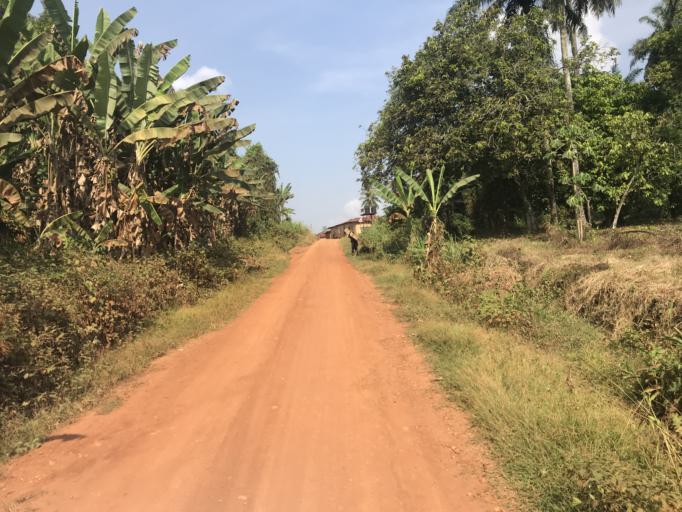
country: NG
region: Osun
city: Osu
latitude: 7.6503
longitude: 4.6640
